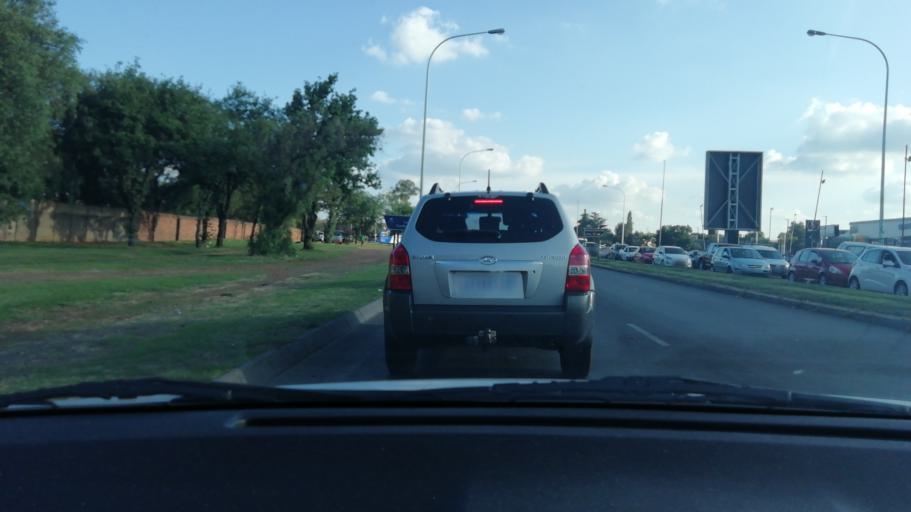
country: ZA
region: Gauteng
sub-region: Ekurhuleni Metropolitan Municipality
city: Boksburg
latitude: -26.1776
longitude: 28.2806
